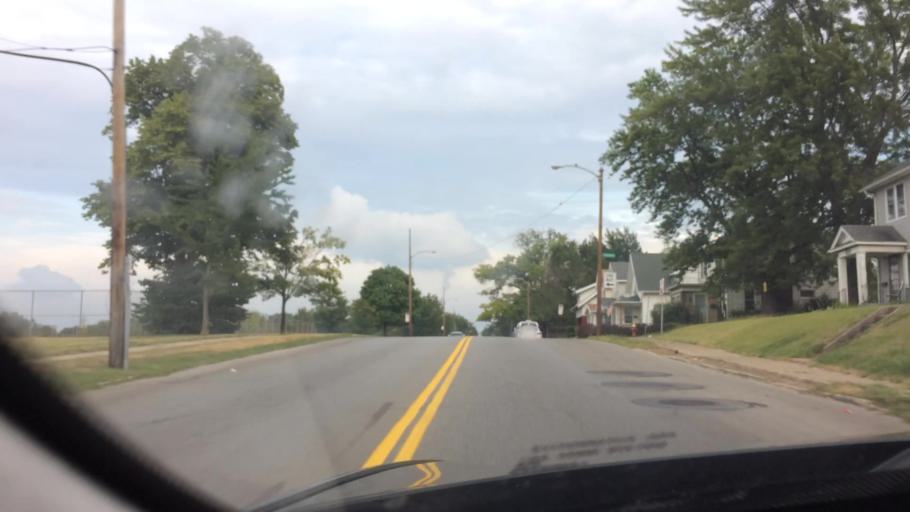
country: US
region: Ohio
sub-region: Wood County
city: Rossford
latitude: 41.6307
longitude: -83.5865
